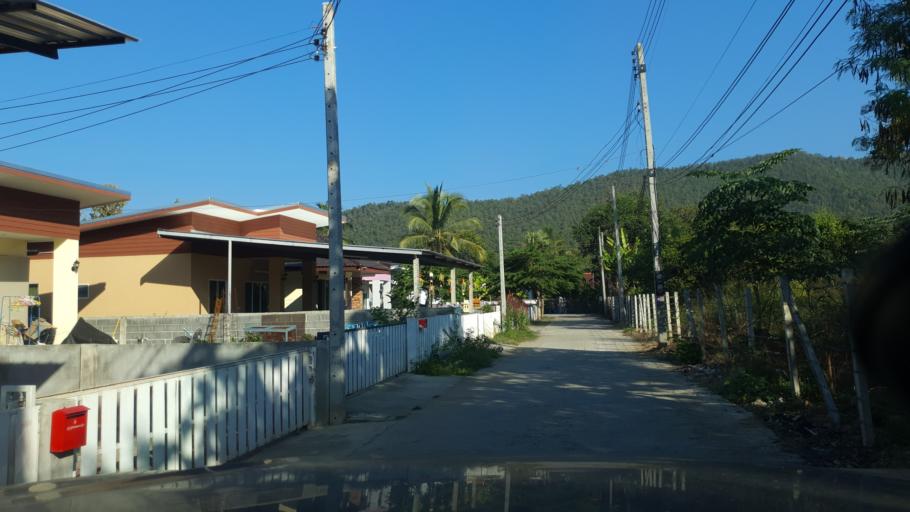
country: TH
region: Chiang Mai
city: Mae On
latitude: 18.7408
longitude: 99.1945
